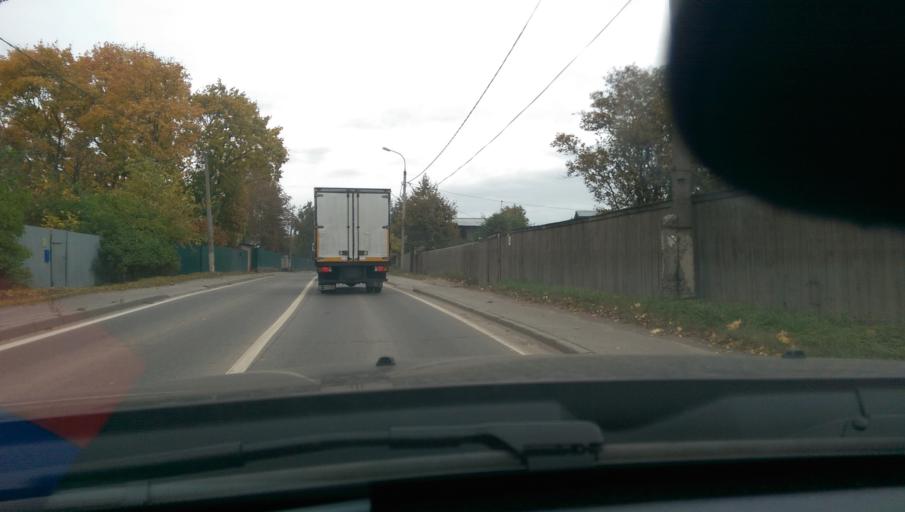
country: RU
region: Moskovskaya
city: Pirogovskiy
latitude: 55.9830
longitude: 37.7273
